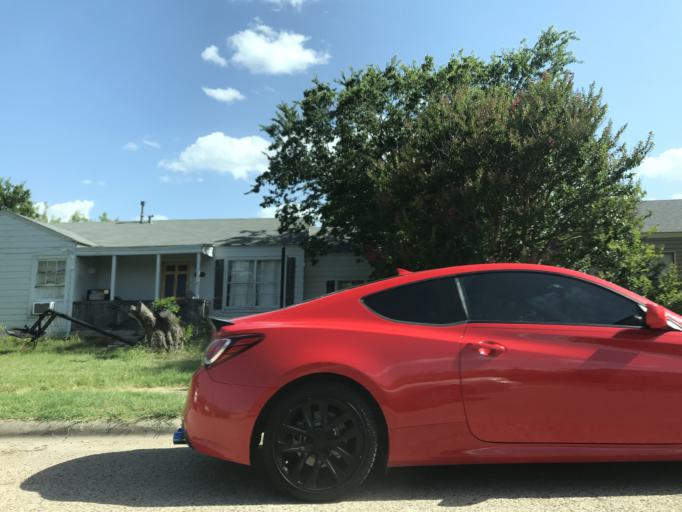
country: US
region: Texas
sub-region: Taylor County
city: Abilene
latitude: 32.4297
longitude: -99.7601
